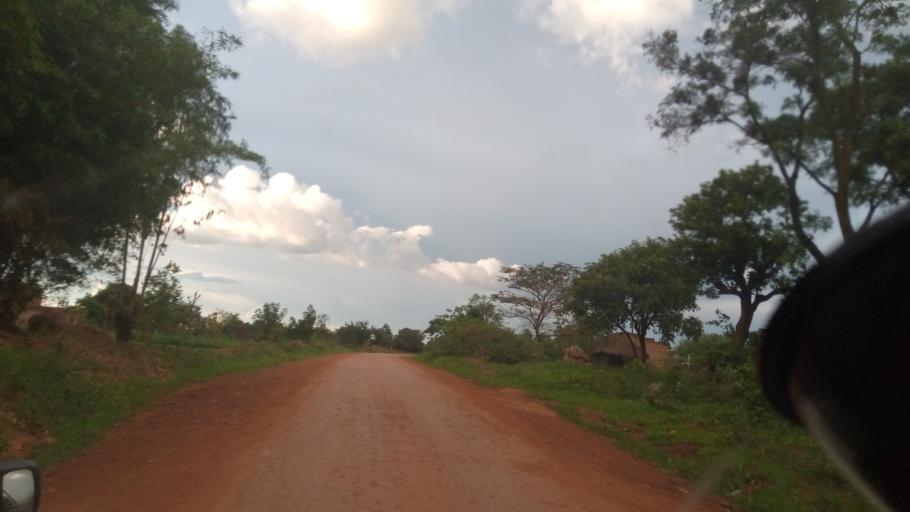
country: UG
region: Northern Region
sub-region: Kole District
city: Kole
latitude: 2.3910
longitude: 32.9335
